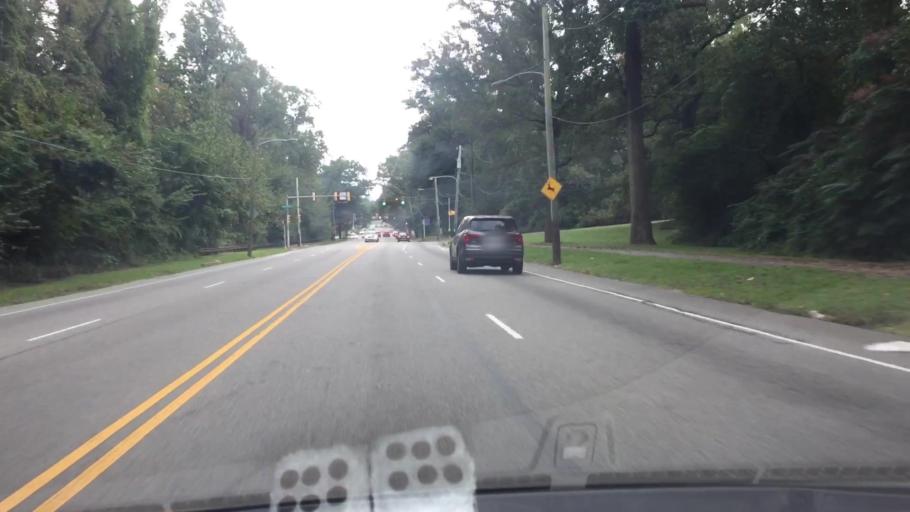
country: US
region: Pennsylvania
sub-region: Montgomery County
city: Bala-Cynwyd
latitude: 39.9887
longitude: -75.2164
